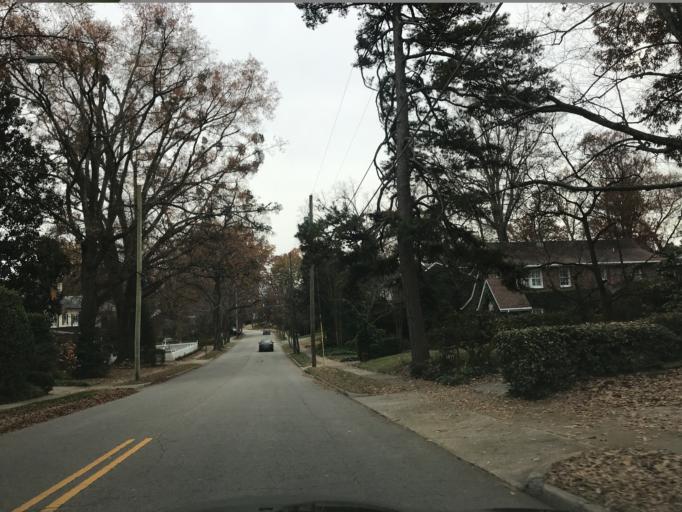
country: US
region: North Carolina
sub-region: Wake County
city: West Raleigh
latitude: 35.8040
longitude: -78.6537
